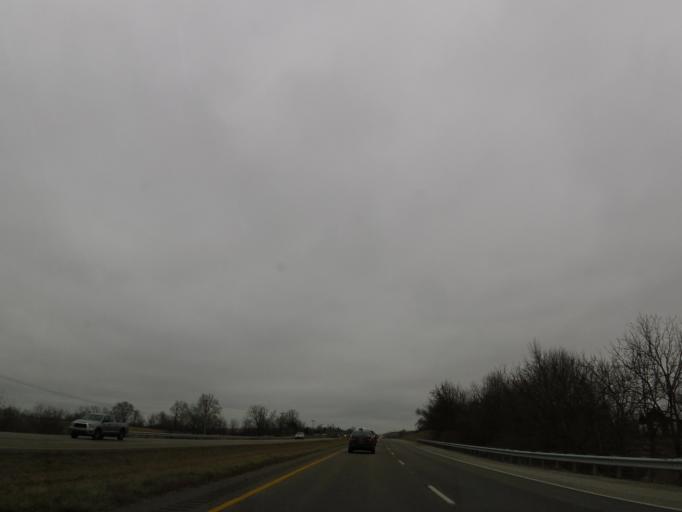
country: US
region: Kentucky
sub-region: Anderson County
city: Lawrenceburg
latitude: 38.0436
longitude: -84.9137
